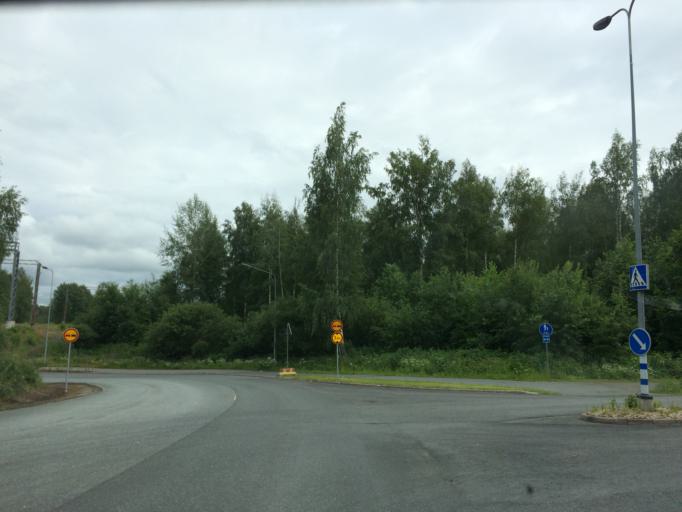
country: FI
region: Haeme
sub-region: Haemeenlinna
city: Haemeenlinna
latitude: 60.9783
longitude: 24.5078
